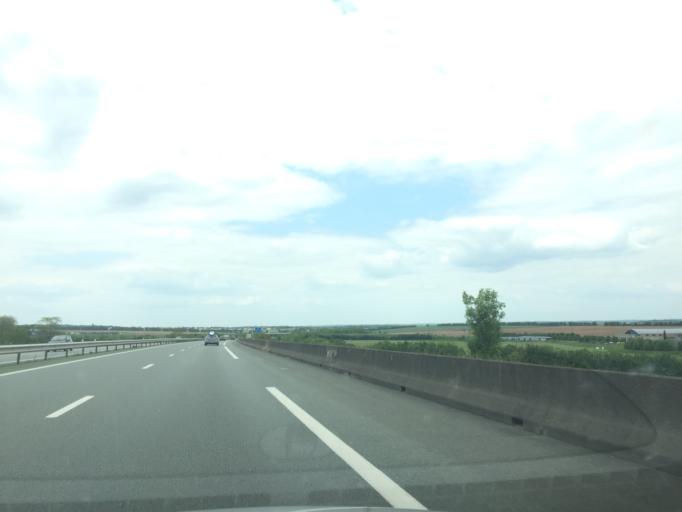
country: FR
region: Poitou-Charentes
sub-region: Departement des Deux-Sevres
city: La Creche
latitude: 46.3510
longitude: -0.3289
